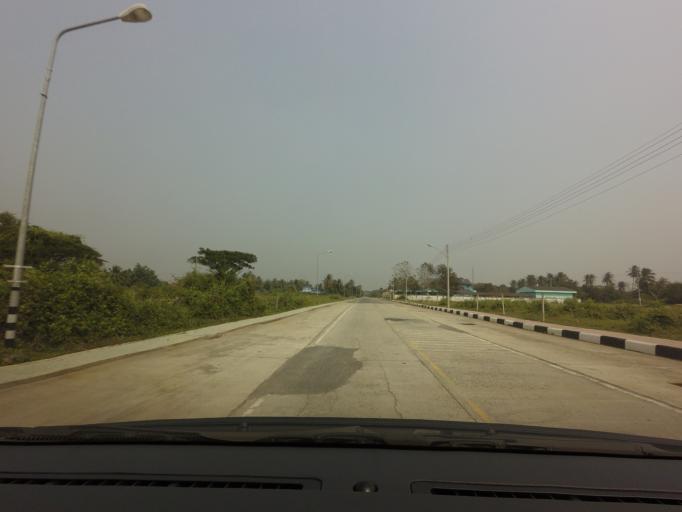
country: TH
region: Prachuap Khiri Khan
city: Kui Buri
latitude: 12.0704
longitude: 99.8655
